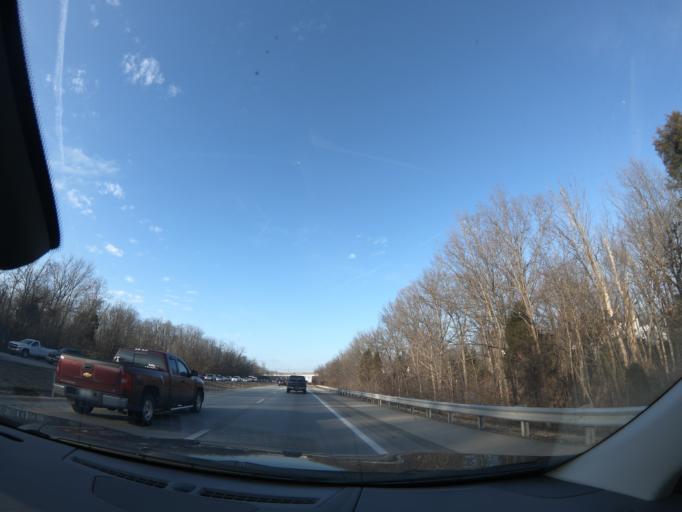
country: US
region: Kentucky
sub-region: Jefferson County
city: Middletown
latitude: 38.2116
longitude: -85.5065
